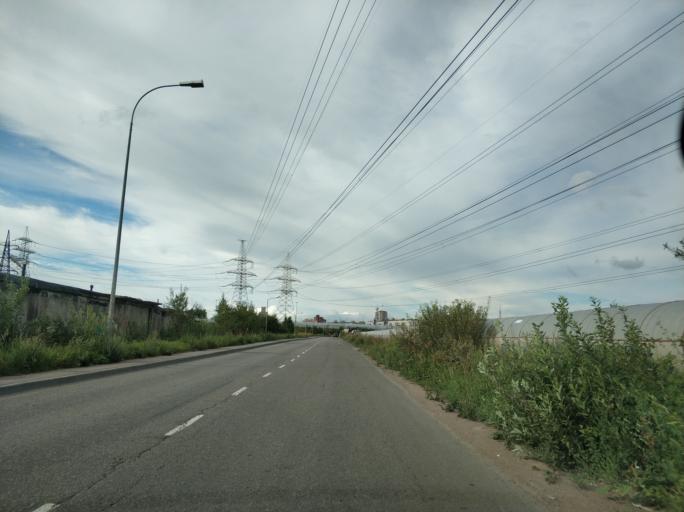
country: RU
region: Leningrad
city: Murino
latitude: 60.0476
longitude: 30.4374
